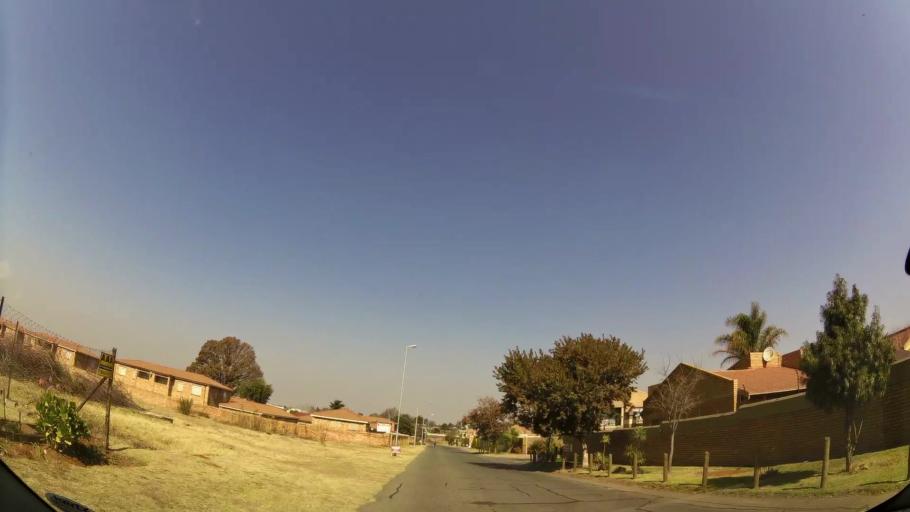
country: ZA
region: Gauteng
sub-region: Ekurhuleni Metropolitan Municipality
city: Boksburg
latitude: -26.1697
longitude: 28.2754
